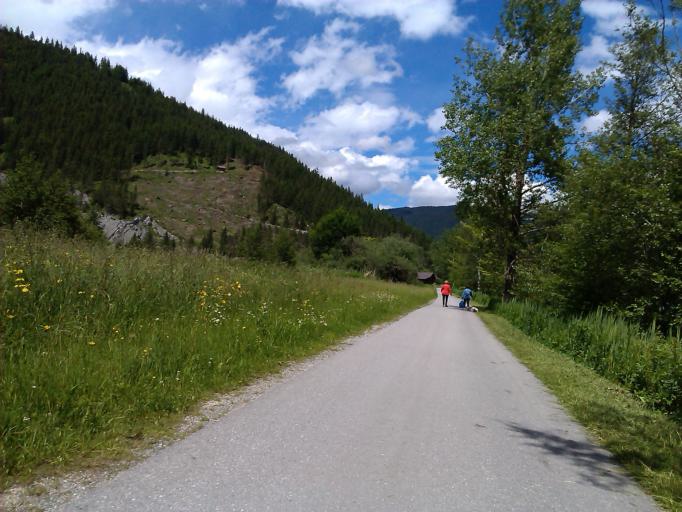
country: AT
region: Tyrol
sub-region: Politischer Bezirk Reutte
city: Ehrwald
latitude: 47.4031
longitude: 10.9068
